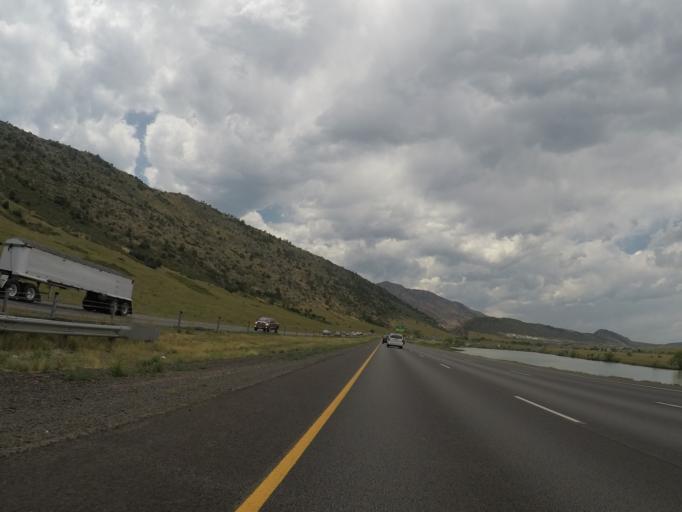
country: US
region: Colorado
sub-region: Jefferson County
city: Indian Hills
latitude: 39.6418
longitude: -105.1738
